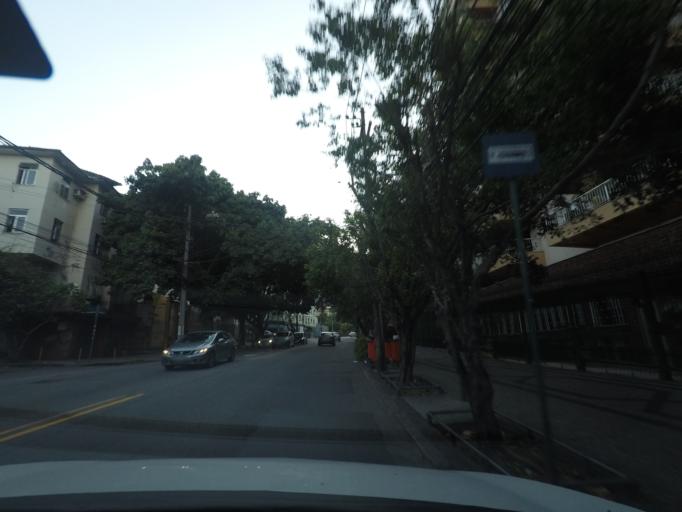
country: BR
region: Rio de Janeiro
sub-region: Rio De Janeiro
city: Rio de Janeiro
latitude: -22.9402
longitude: -43.2495
